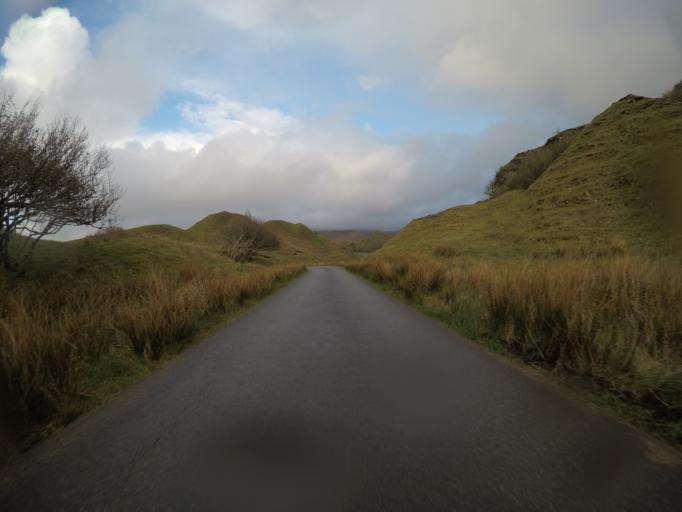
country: GB
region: Scotland
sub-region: Highland
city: Portree
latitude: 57.5839
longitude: -6.3279
